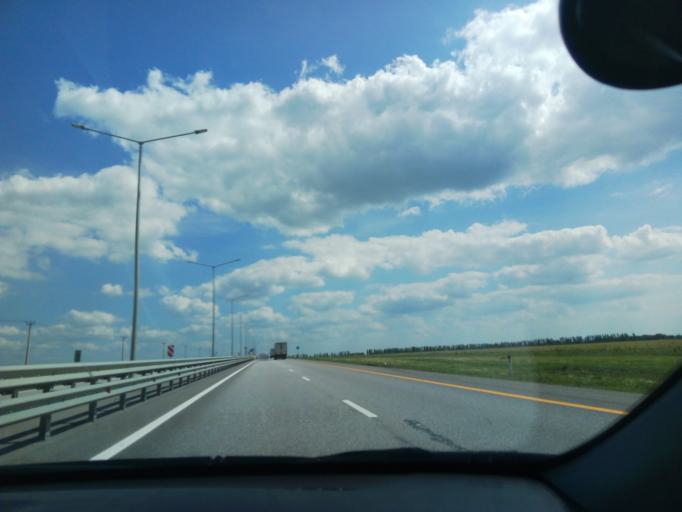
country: RU
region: Voronezj
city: Kashirskoye
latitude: 51.4907
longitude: 39.5306
